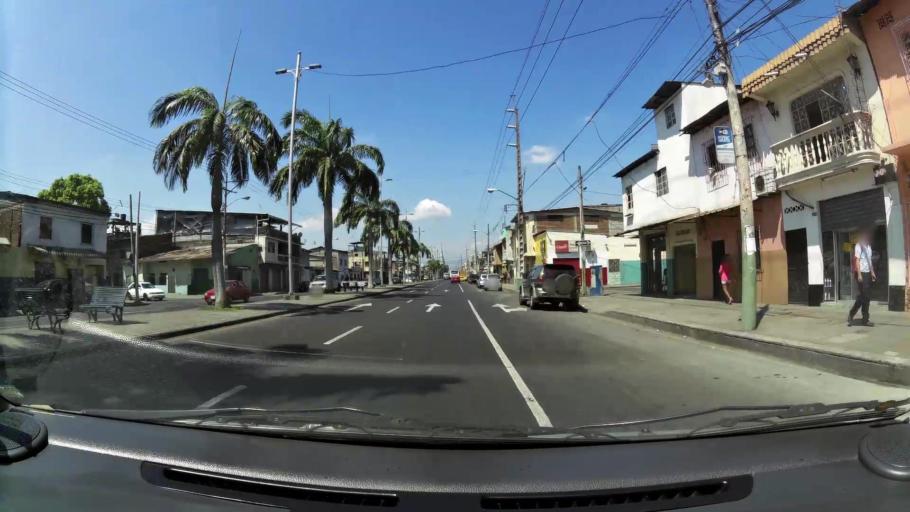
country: EC
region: Guayas
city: Guayaquil
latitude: -2.1988
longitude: -79.9283
